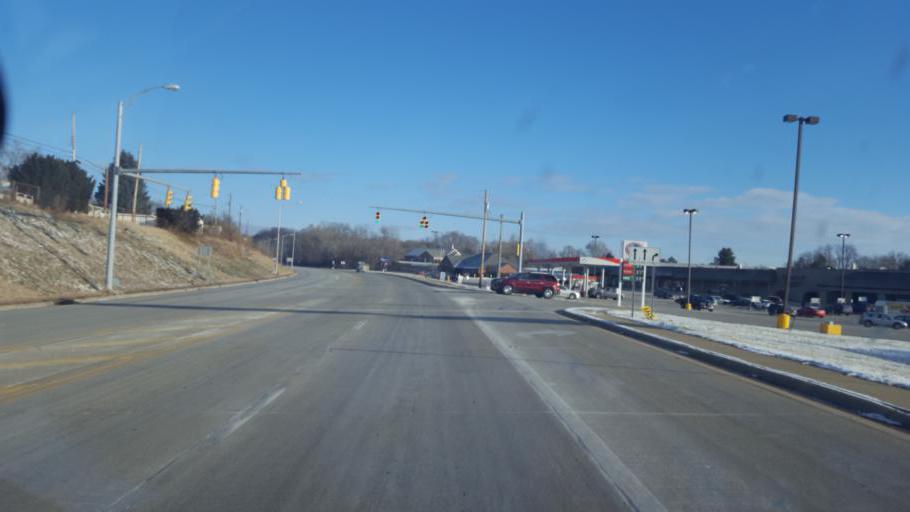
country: US
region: Ohio
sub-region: Pike County
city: Waverly
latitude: 39.1326
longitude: -82.9786
